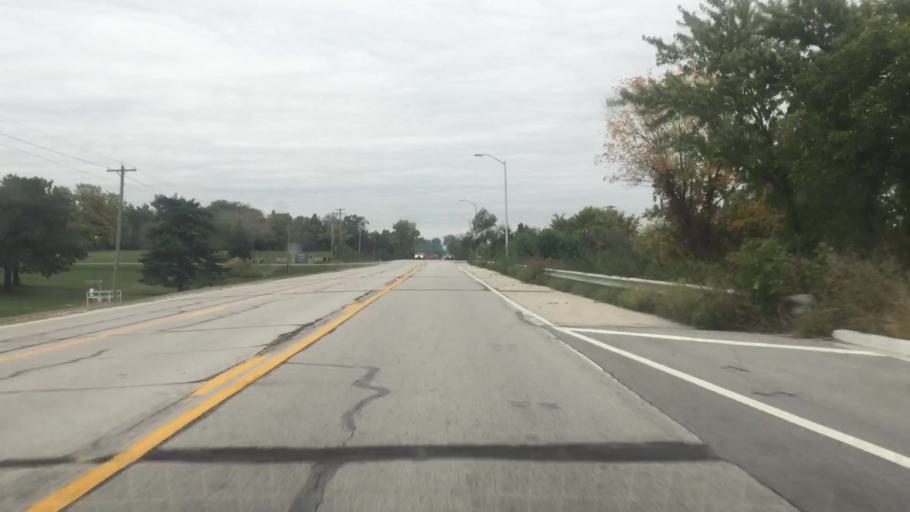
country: US
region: Kansas
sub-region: Johnson County
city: Lenexa
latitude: 38.9884
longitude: -94.7798
